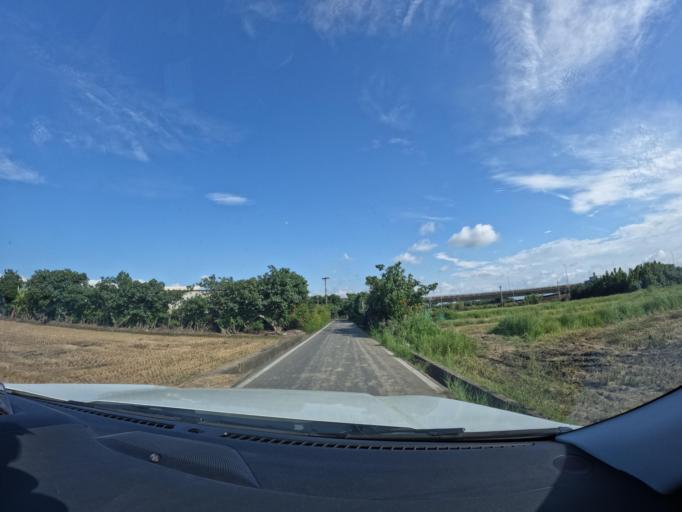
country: TW
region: Taiwan
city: Taoyuan City
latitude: 25.0843
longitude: 121.1784
